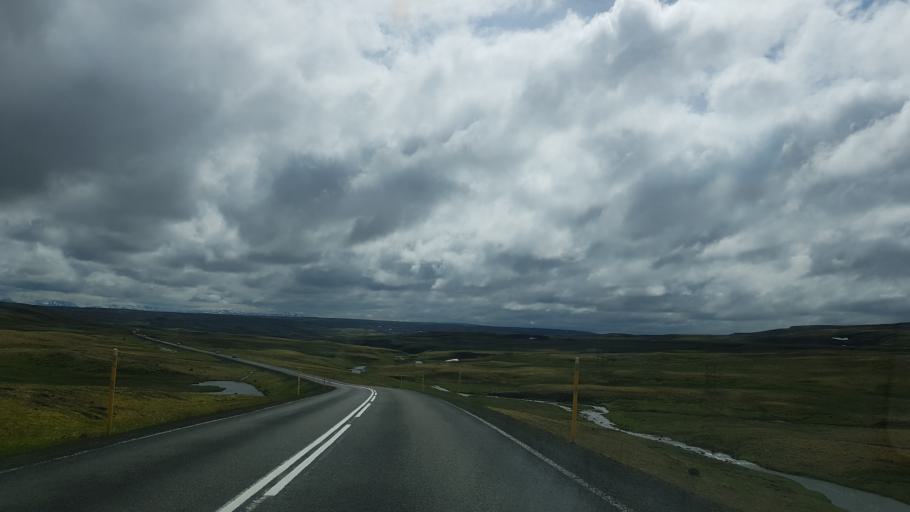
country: IS
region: West
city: Borgarnes
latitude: 64.9722
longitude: -21.0679
